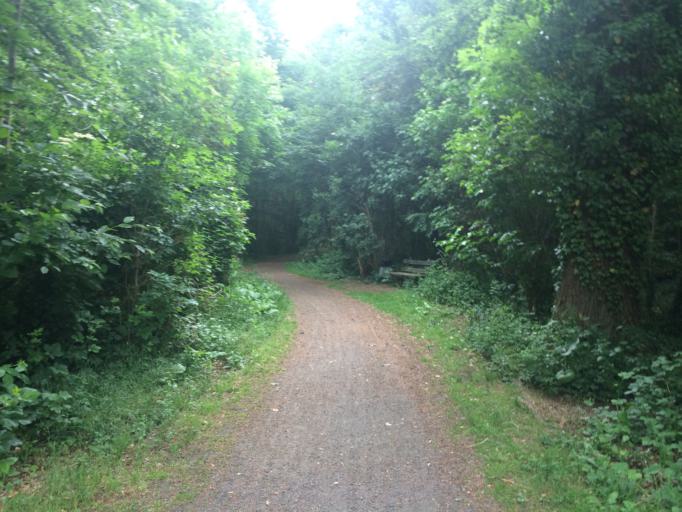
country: DE
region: Hesse
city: Dieburg
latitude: 49.8953
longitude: 8.8557
